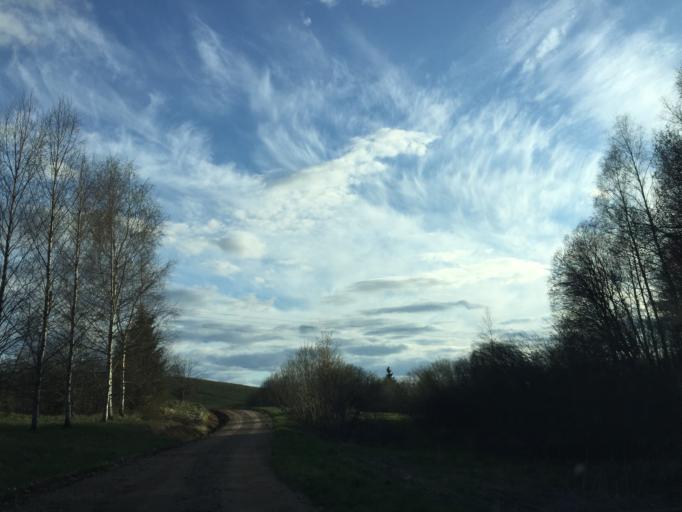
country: LV
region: Rezekne
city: Rezekne
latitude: 56.5820
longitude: 27.3426
